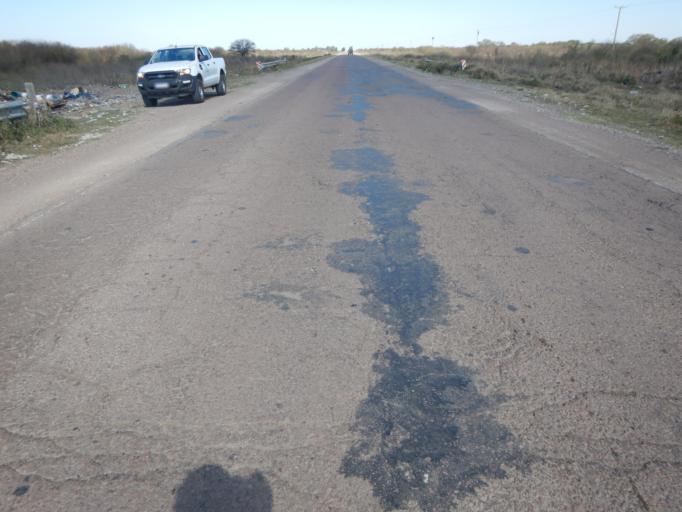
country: AR
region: Santiago del Estero
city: Los Juries
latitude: -28.6508
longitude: -61.5267
